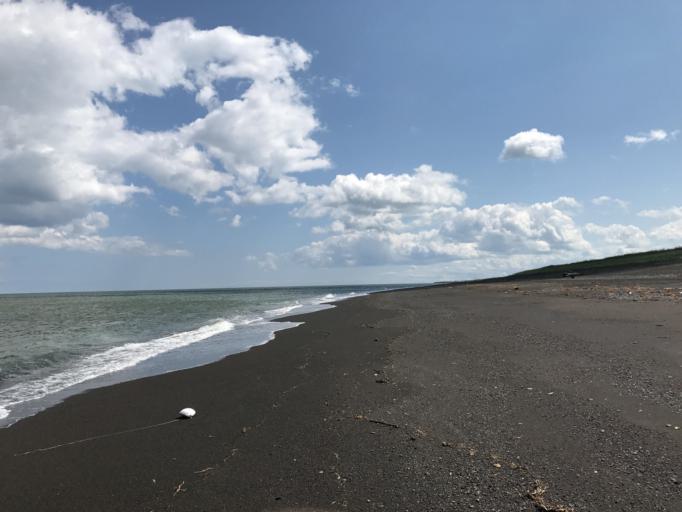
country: JP
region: Hokkaido
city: Mombetsu
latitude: 44.3930
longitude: 143.2930
